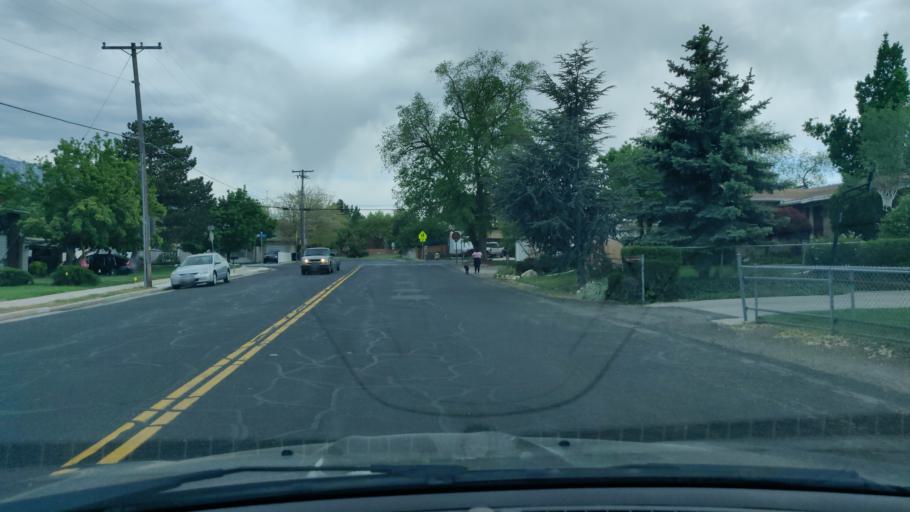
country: US
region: Utah
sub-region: Salt Lake County
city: Little Cottonwood Creek Valley
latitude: 40.6209
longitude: -111.8440
